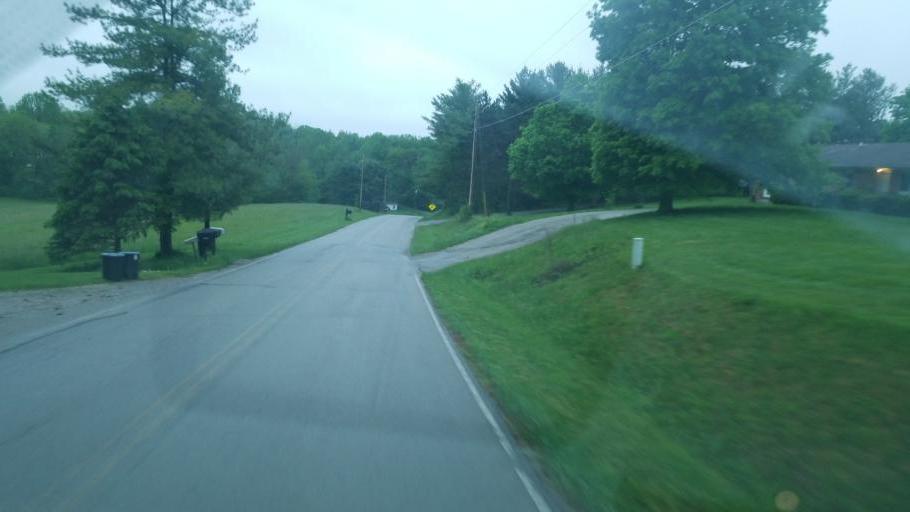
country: US
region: Ohio
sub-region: Highland County
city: Hillsboro
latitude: 39.1709
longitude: -83.6285
